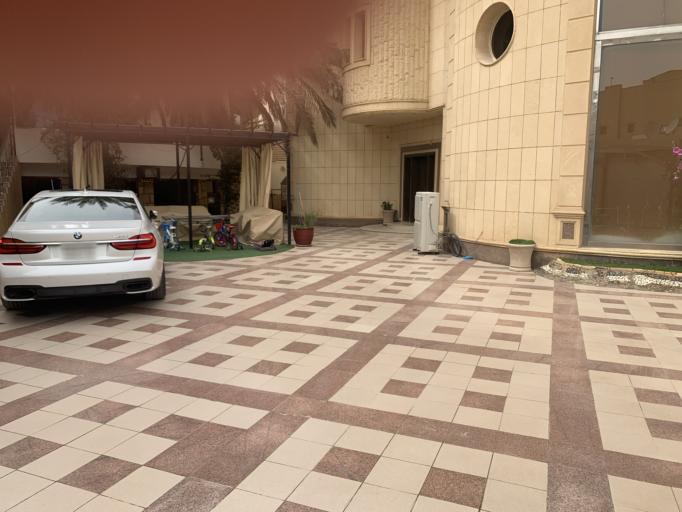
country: SA
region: Ar Riyad
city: Riyadh
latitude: 24.7780
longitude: 46.6525
